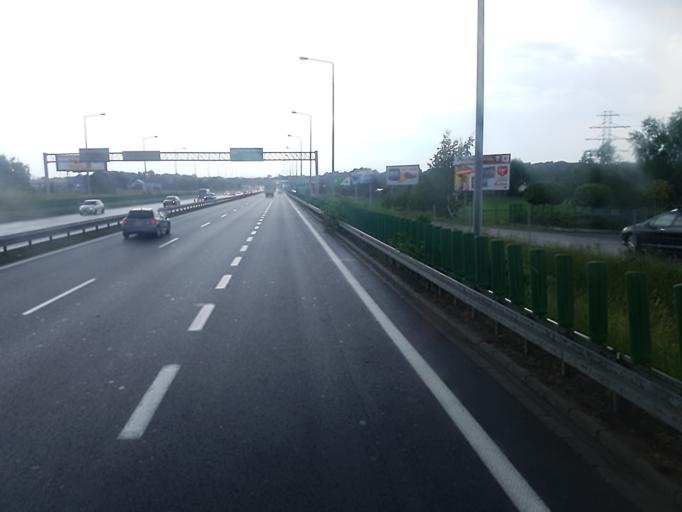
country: PL
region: Silesian Voivodeship
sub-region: Powiat bielski
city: Mazancowice
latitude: 49.8388
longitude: 18.9947
